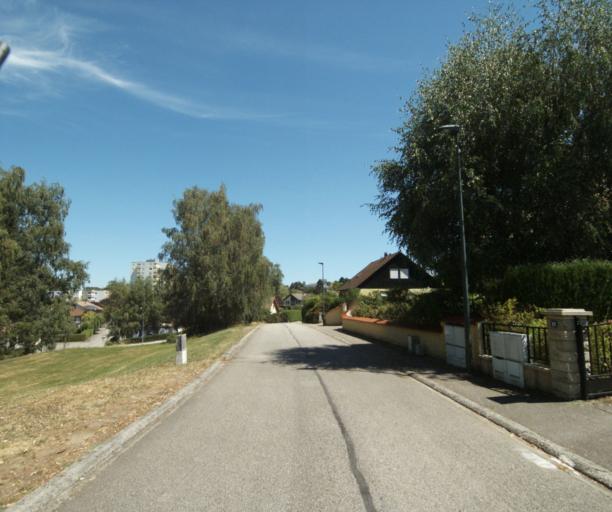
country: FR
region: Lorraine
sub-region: Departement des Vosges
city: Epinal
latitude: 48.1916
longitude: 6.4533
